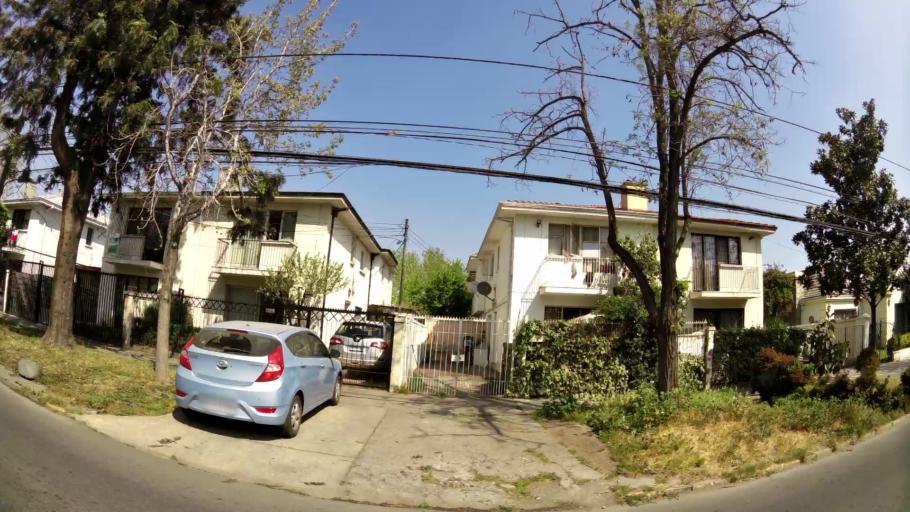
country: CL
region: Santiago Metropolitan
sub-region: Provincia de Santiago
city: Villa Presidente Frei, Nunoa, Santiago, Chile
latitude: -33.4578
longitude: -70.6107
